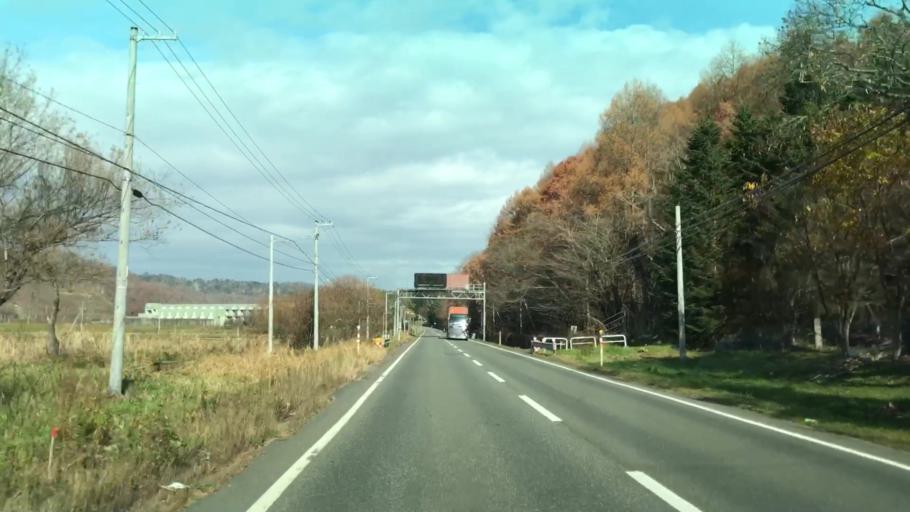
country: JP
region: Hokkaido
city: Shizunai-furukawacho
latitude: 42.6192
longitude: 142.1503
